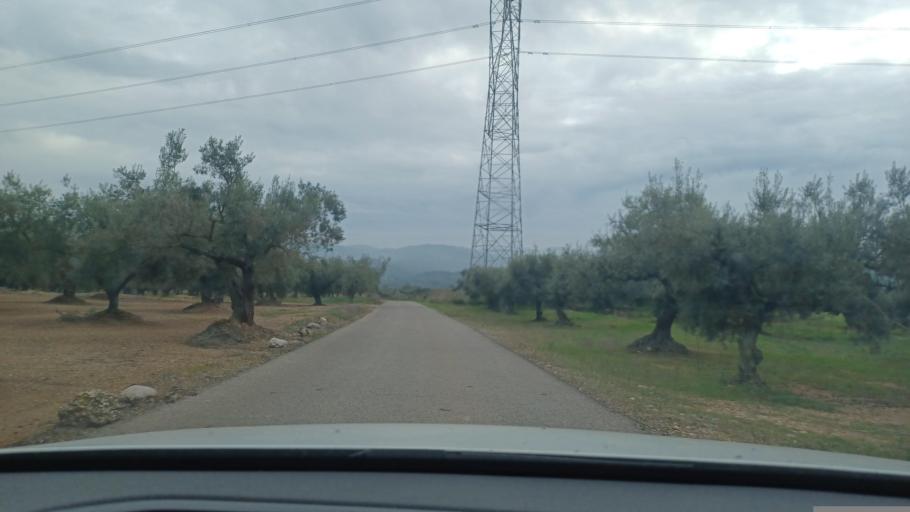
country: ES
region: Catalonia
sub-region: Provincia de Tarragona
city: Santa Barbara
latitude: 40.6687
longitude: 0.4396
